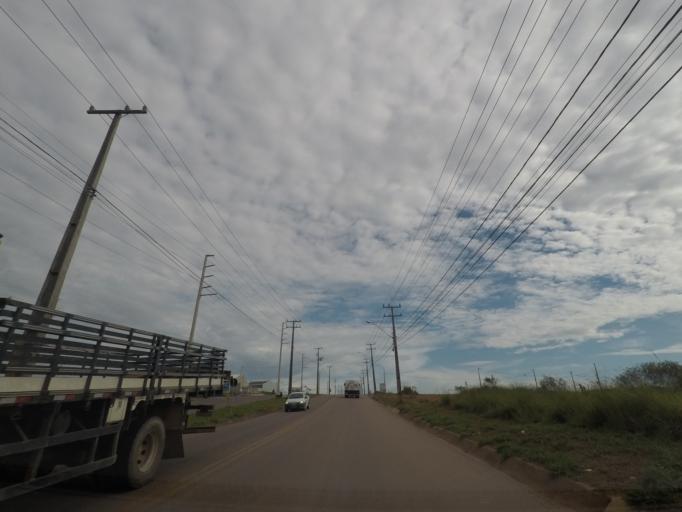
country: BR
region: Parana
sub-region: Araucaria
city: Araucaria
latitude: -25.6322
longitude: -49.2913
